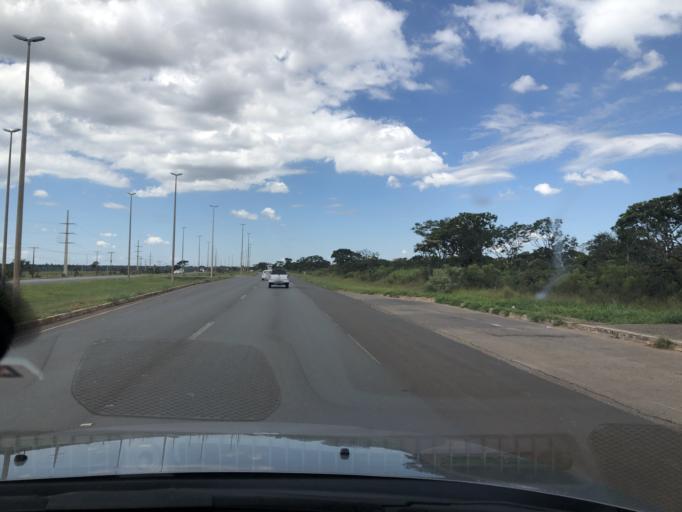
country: BR
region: Federal District
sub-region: Brasilia
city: Brasilia
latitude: -15.9695
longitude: -48.0179
